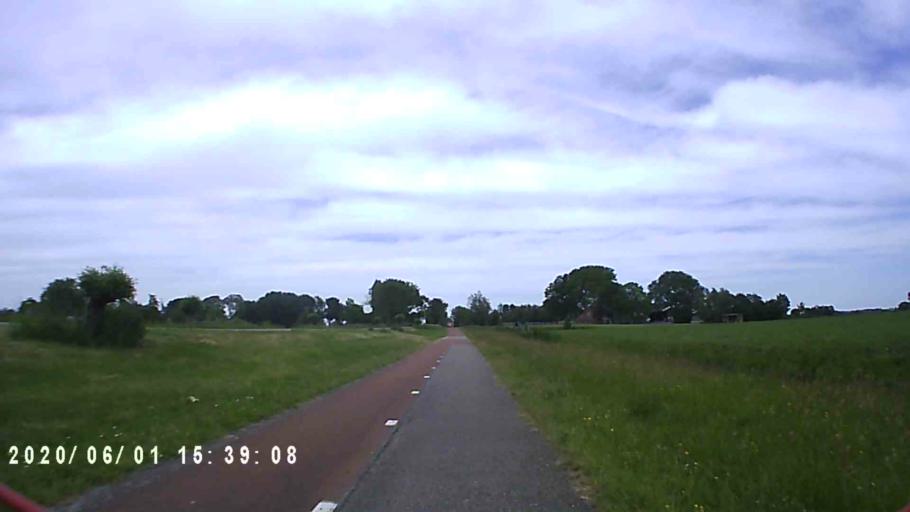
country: NL
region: Friesland
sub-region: Gemeente Leeuwarden
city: Wirdum
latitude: 53.1525
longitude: 5.8156
